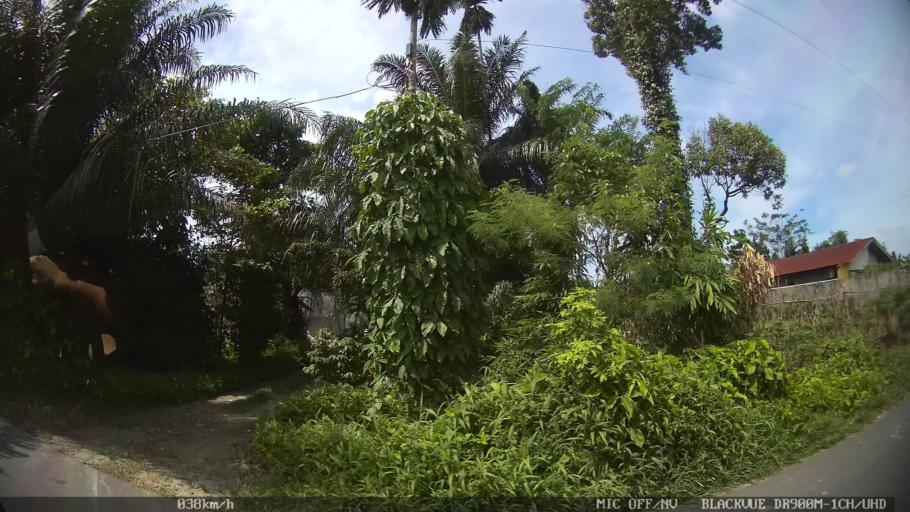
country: ID
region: North Sumatra
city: Percut
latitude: 3.5892
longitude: 98.8696
